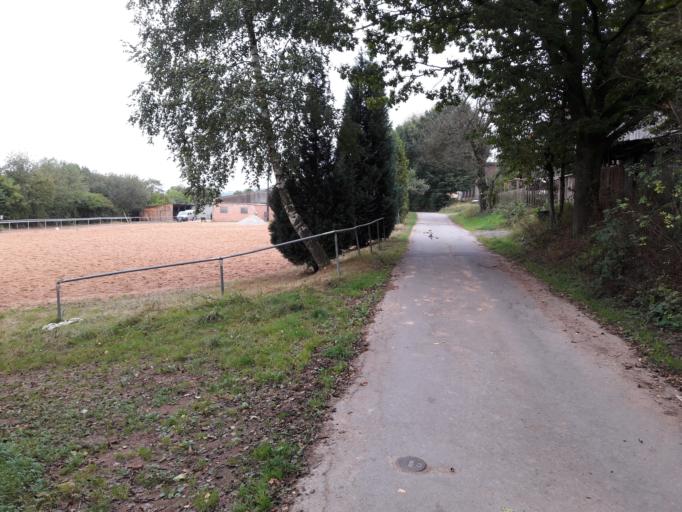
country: DE
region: Saarland
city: Ottweiler
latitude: 49.4044
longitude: 7.1442
